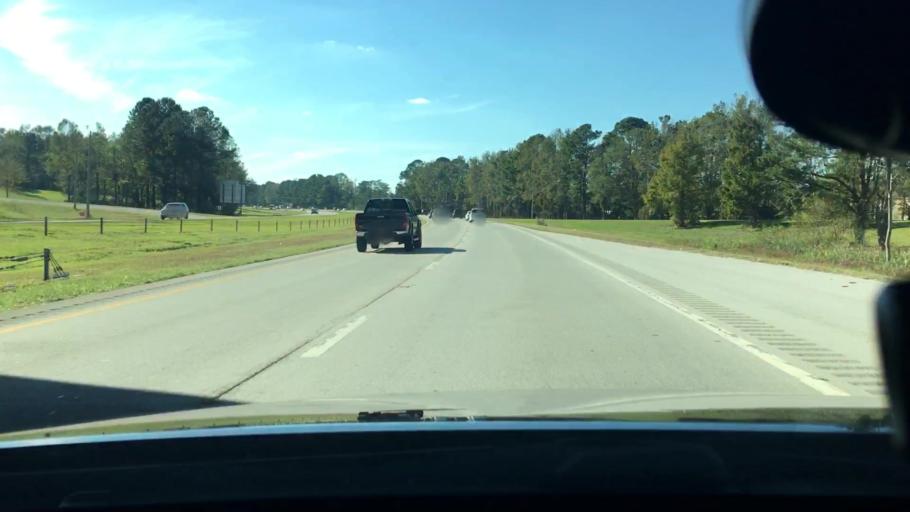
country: US
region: North Carolina
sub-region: Craven County
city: New Bern
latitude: 35.1012
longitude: -77.0587
